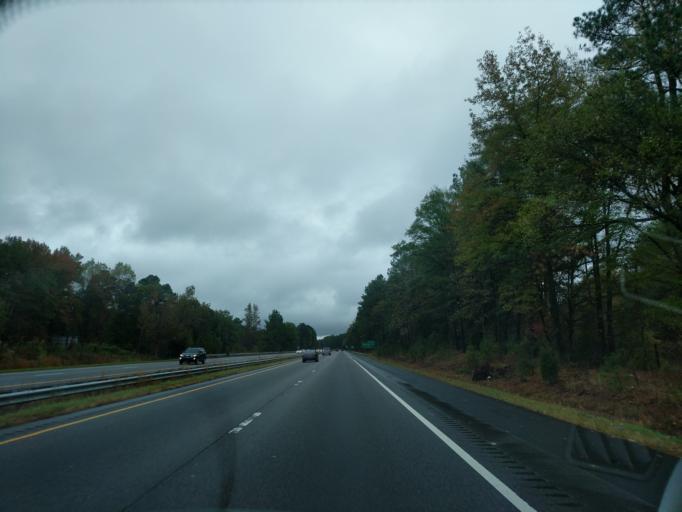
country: US
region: North Carolina
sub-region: Durham County
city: Gorman
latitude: 36.0354
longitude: -78.8340
